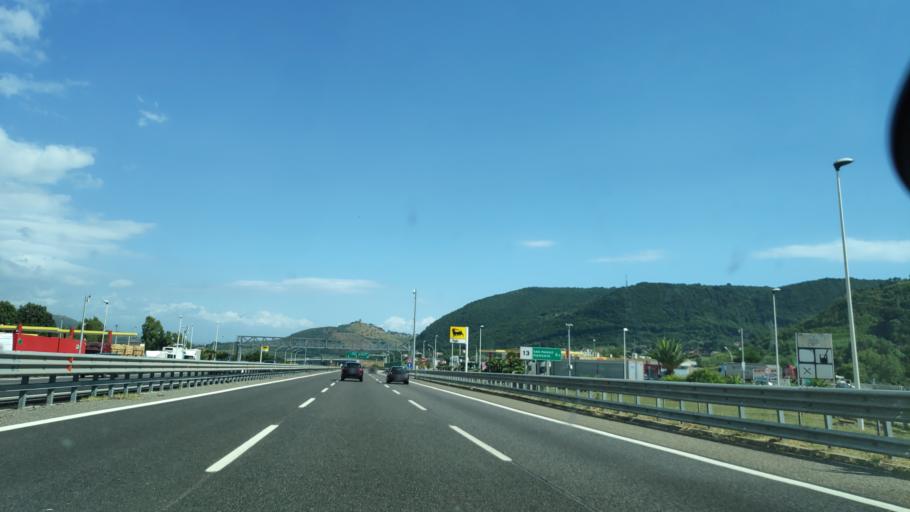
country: IT
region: Campania
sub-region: Provincia di Salerno
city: San Mango Piemonte
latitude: 40.6938
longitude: 14.8337
